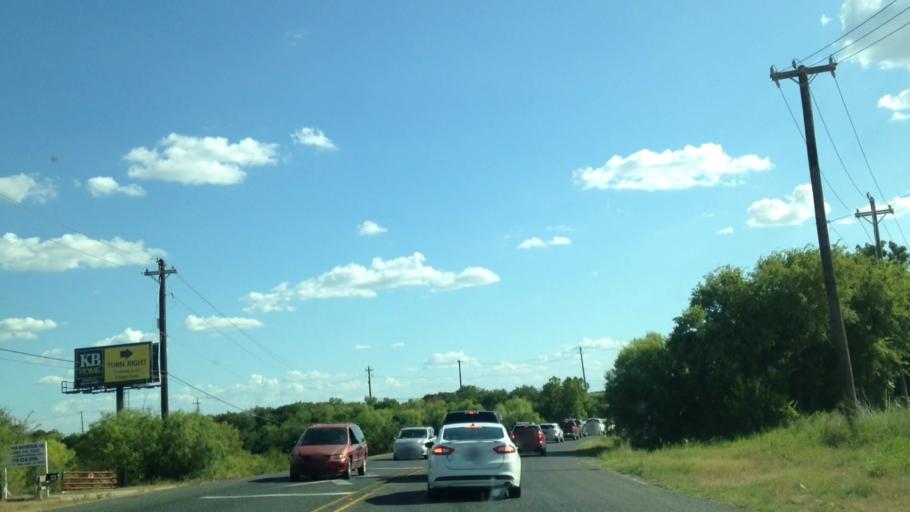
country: US
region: Texas
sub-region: Bexar County
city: Selma
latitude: 29.6064
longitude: -98.3262
